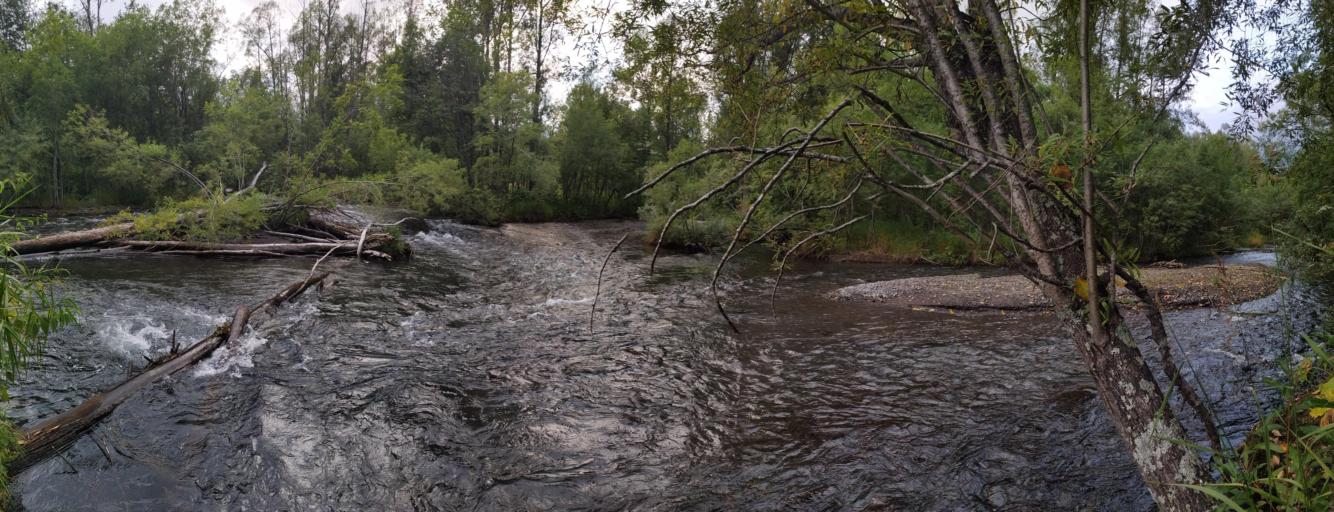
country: RU
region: Kamtsjatka
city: Yelizovo
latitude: 53.8112
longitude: 158.0950
